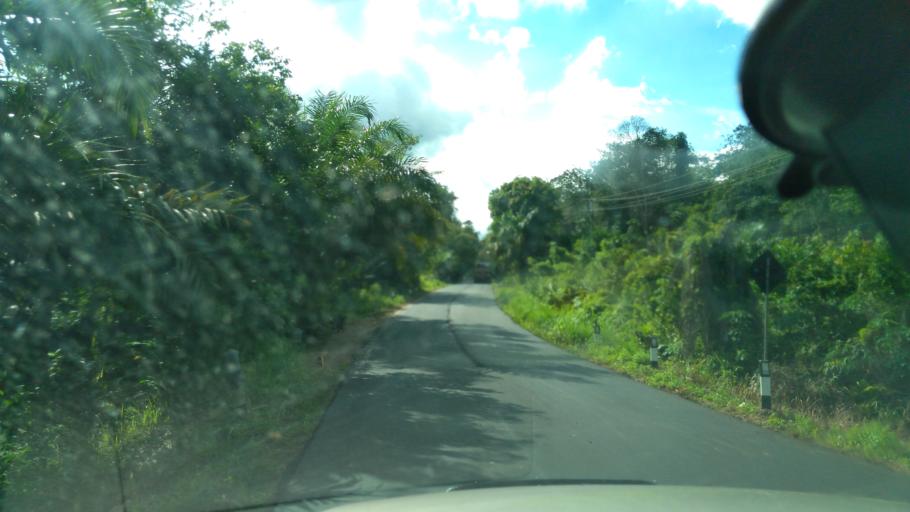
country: ID
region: West Kalimantan
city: Tayan
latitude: 0.3676
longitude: 109.9890
